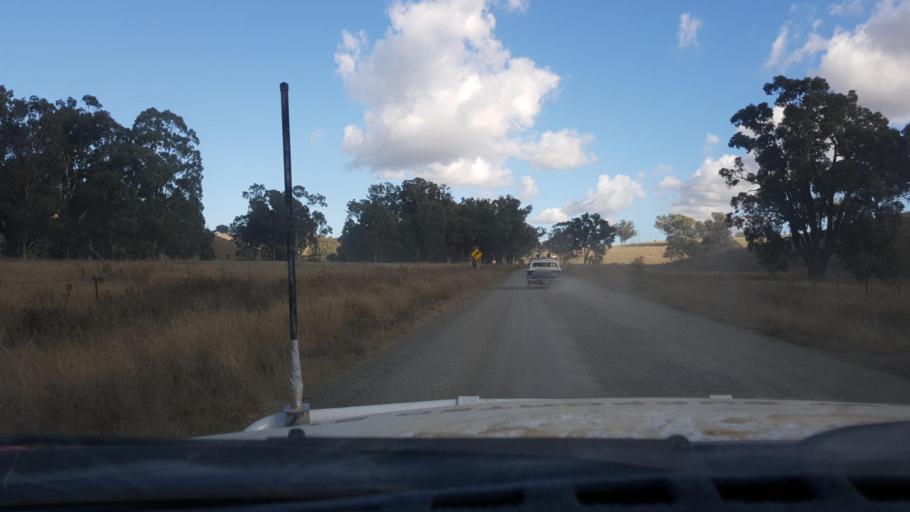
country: AU
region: New South Wales
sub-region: Tamworth Municipality
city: Manilla
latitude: -30.6130
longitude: 150.5125
